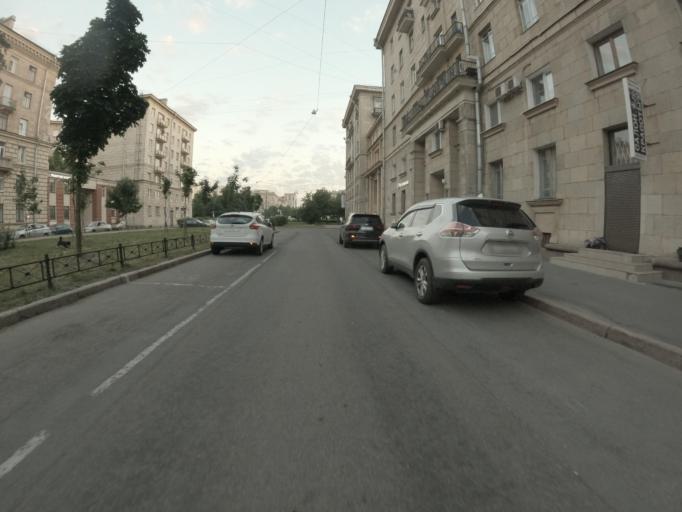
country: RU
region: St.-Petersburg
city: Kupchino
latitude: 59.8627
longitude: 30.3224
